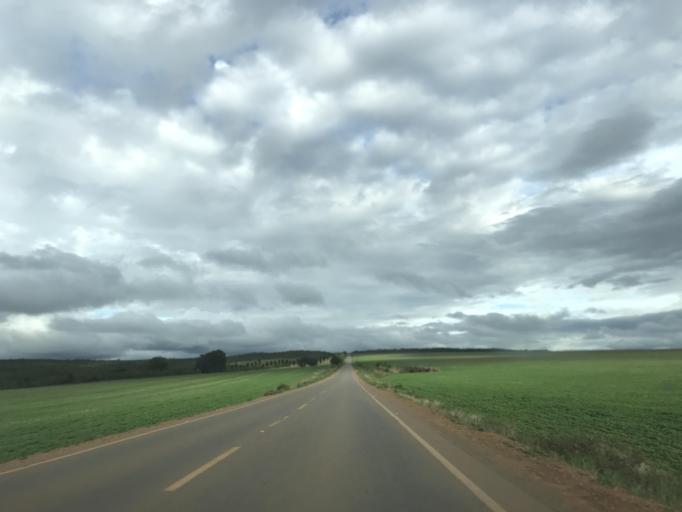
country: BR
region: Goias
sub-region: Vianopolis
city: Vianopolis
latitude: -16.5765
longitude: -48.3175
